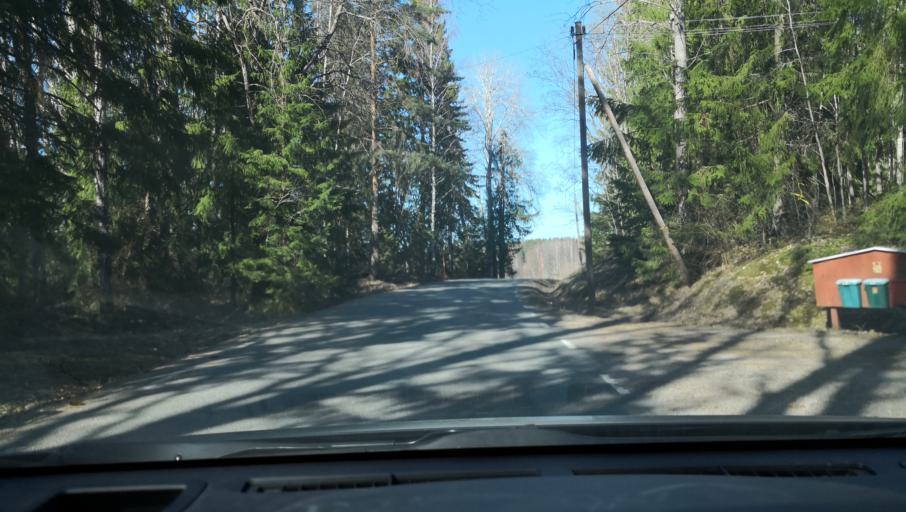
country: SE
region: Vaestmanland
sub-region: Sala Kommun
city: Sala
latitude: 59.9746
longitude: 16.4682
